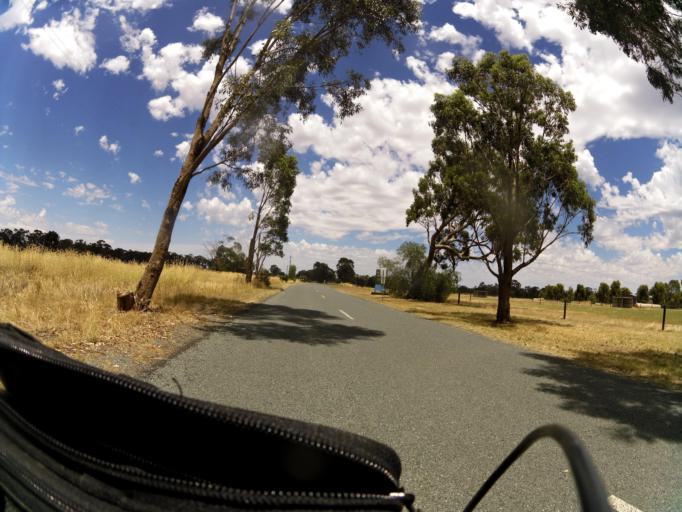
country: AU
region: Victoria
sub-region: Greater Shepparton
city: Shepparton
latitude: -36.6252
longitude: 145.2136
